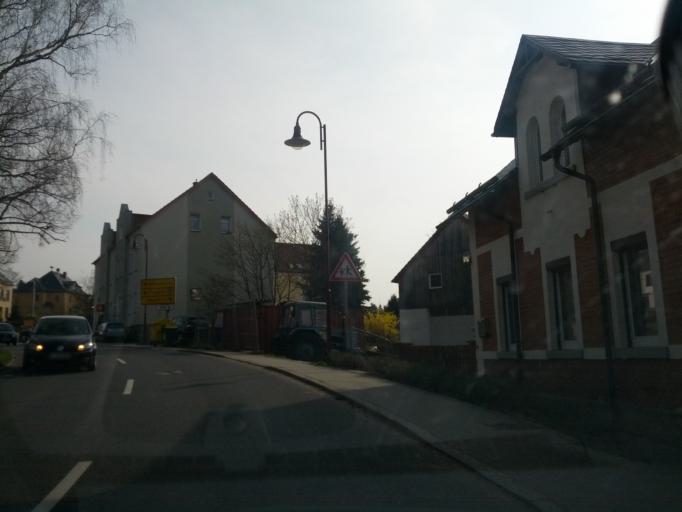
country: DE
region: Saxony
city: Stutzengrun
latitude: 50.5670
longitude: 12.5285
